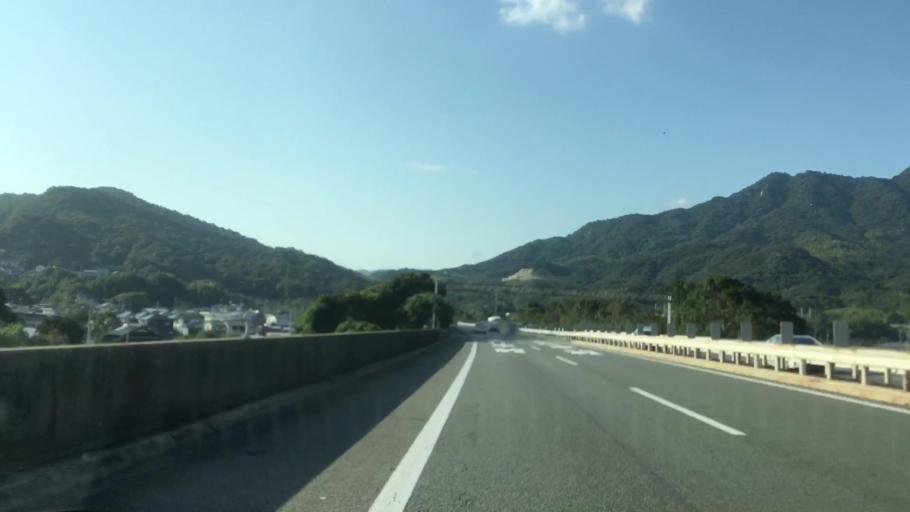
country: JP
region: Yamaguchi
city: Hofu
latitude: 34.0660
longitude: 131.6041
